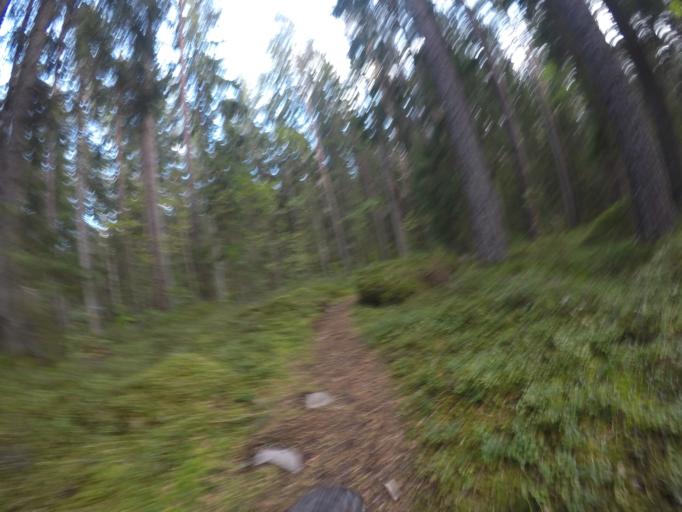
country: SE
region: Vaestmanland
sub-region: Kopings Kommun
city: Koping
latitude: 59.5346
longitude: 15.9983
